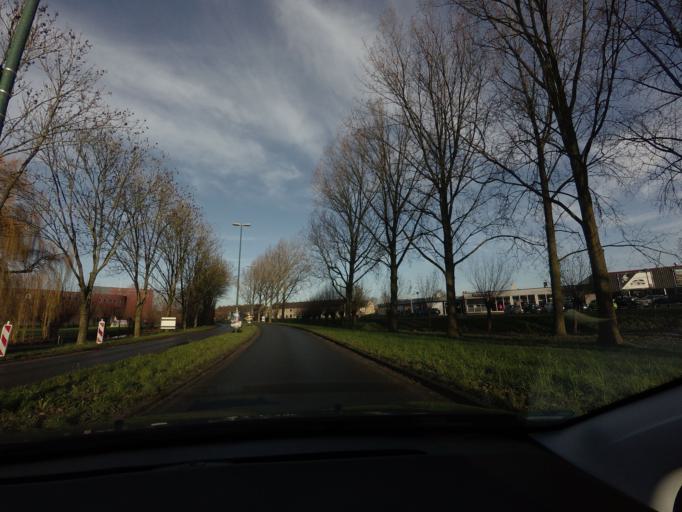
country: NL
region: Utrecht
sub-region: Gemeente Woerden
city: Woerden
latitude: 52.0795
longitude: 4.8776
